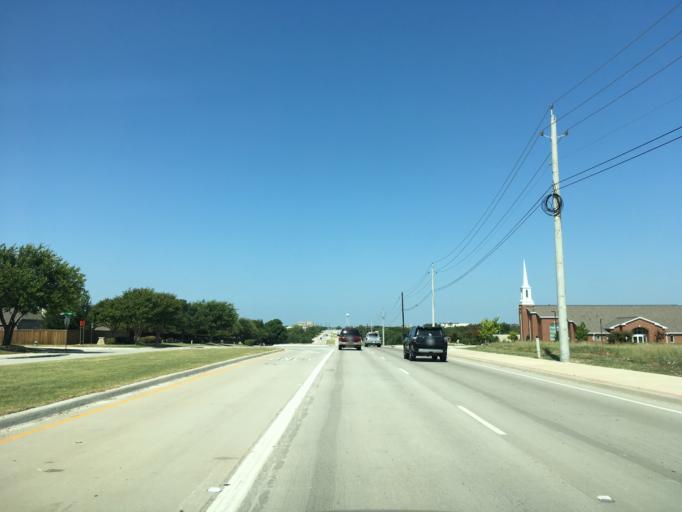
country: US
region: Texas
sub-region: Collin County
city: Fairview
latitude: 33.1296
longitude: -96.6308
